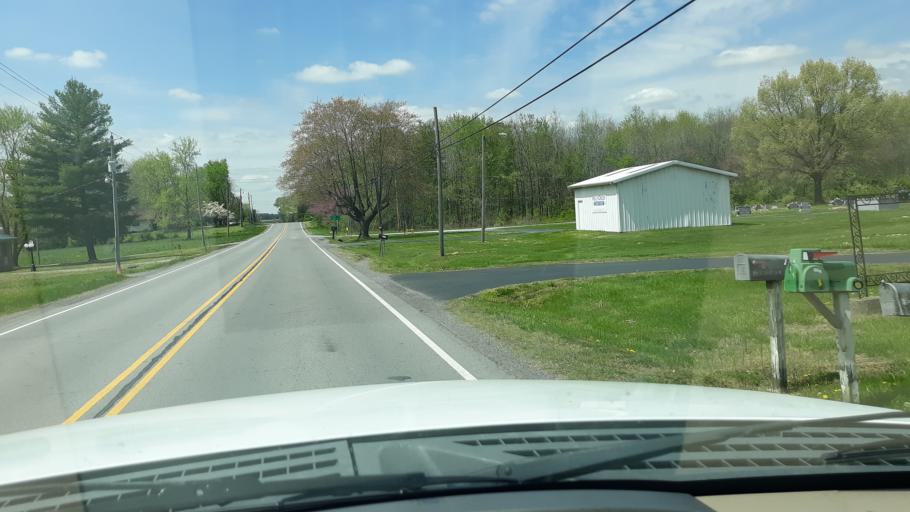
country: US
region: Illinois
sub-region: Saline County
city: Eldorado
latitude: 37.8190
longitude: -88.4587
